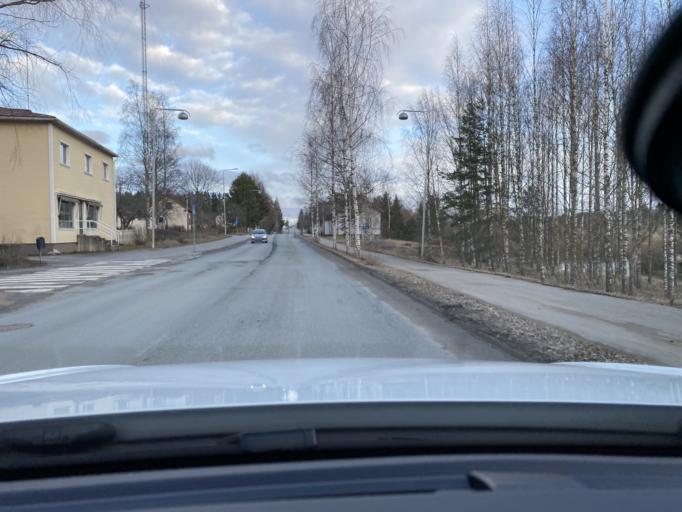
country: FI
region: Pirkanmaa
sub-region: Lounais-Pirkanmaa
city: Punkalaidun
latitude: 61.1163
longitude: 23.0896
